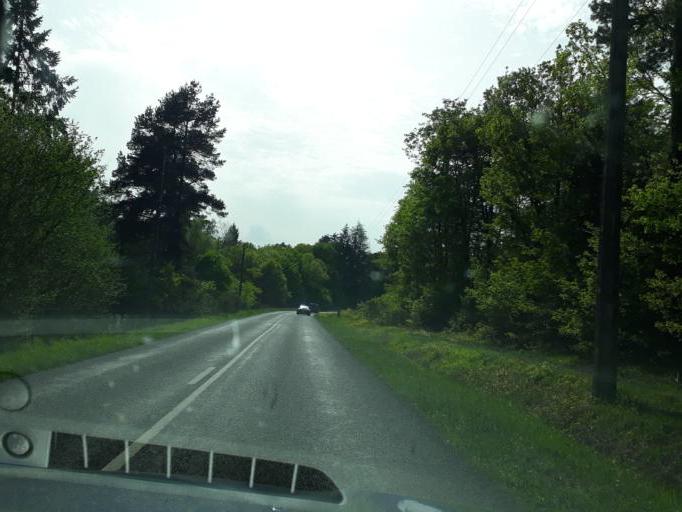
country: FR
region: Centre
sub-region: Departement du Loir-et-Cher
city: Saint-Laurent-Nouan
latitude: 47.6554
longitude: 1.6271
